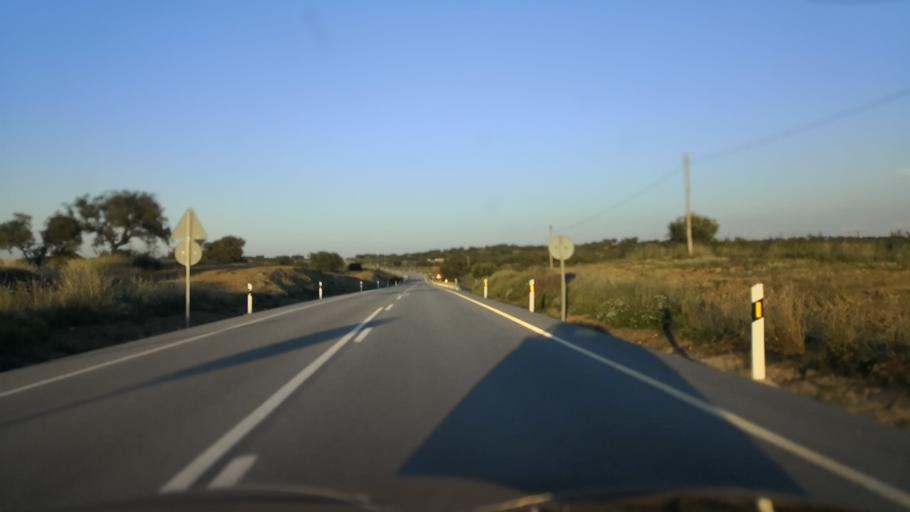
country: ES
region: Extremadura
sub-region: Provincia de Caceres
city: Salorino
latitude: 39.5134
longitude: -7.0875
